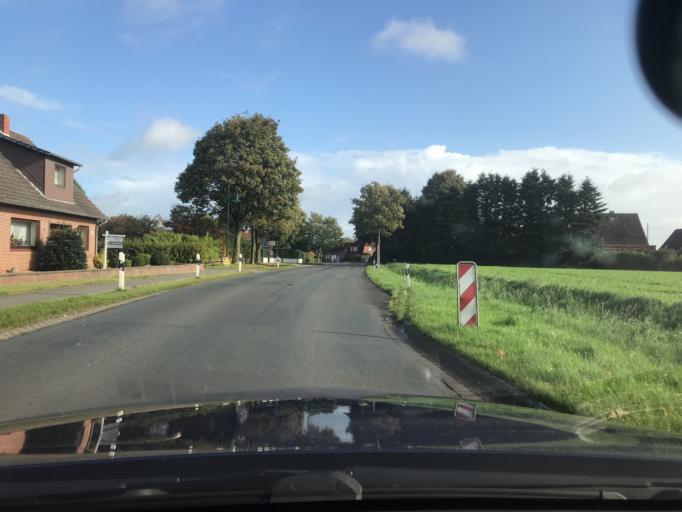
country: DE
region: Lower Saxony
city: Ahlerstedt
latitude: 53.4325
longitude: 9.4607
